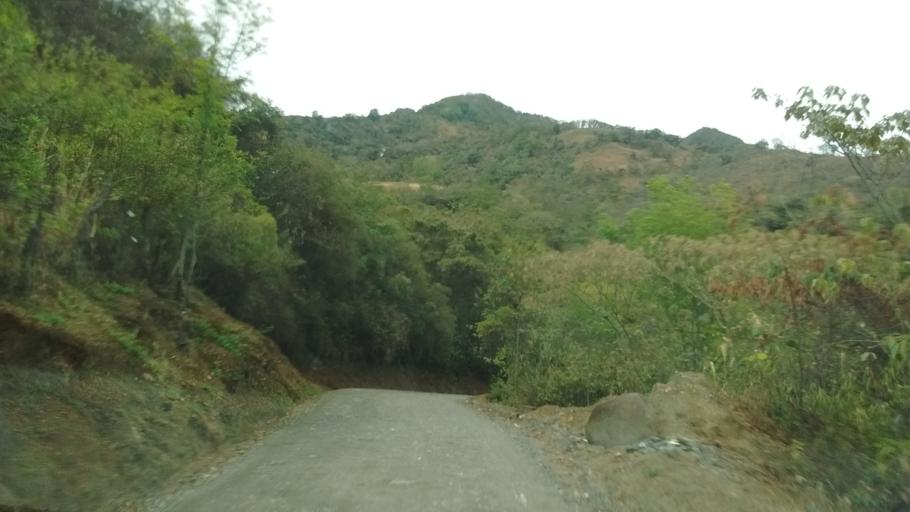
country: CO
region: Cauca
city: Almaguer
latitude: 1.8542
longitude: -76.9289
